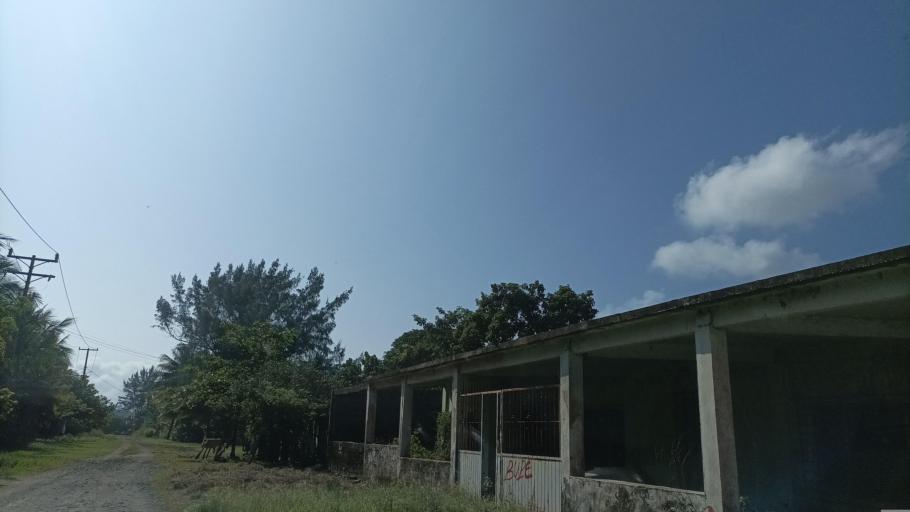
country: MX
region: Veracruz
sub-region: Coatzacoalcos
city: Fraccionamiento Ciudad Olmeca
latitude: 18.2086
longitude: -94.6101
